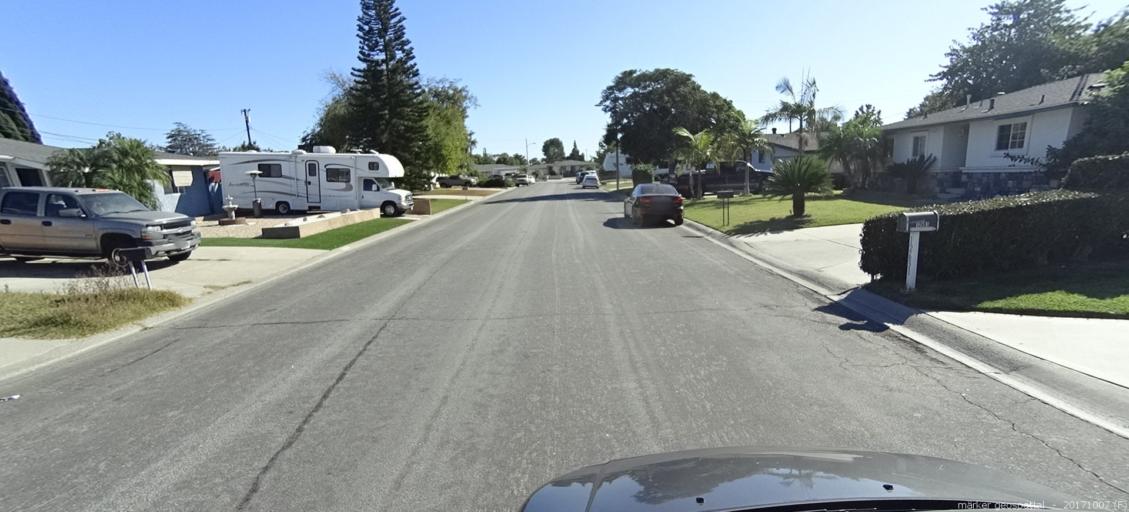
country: US
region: California
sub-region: Orange County
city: Garden Grove
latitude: 33.7794
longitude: -117.9709
